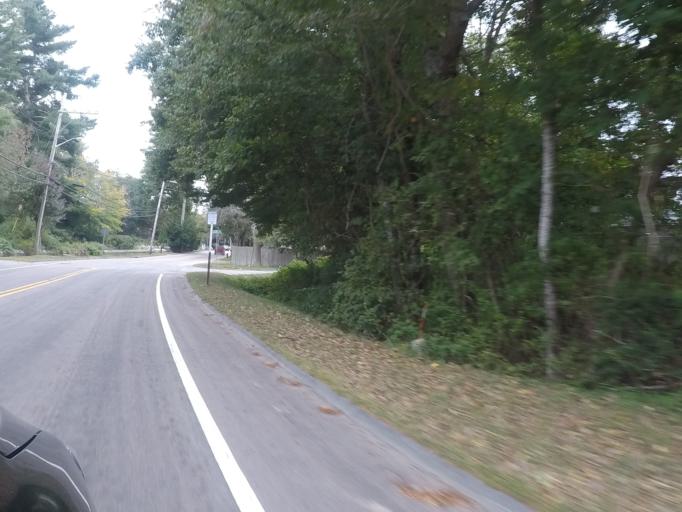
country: US
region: Massachusetts
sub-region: Bristol County
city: Smith Mills
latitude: 41.6323
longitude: -70.9914
